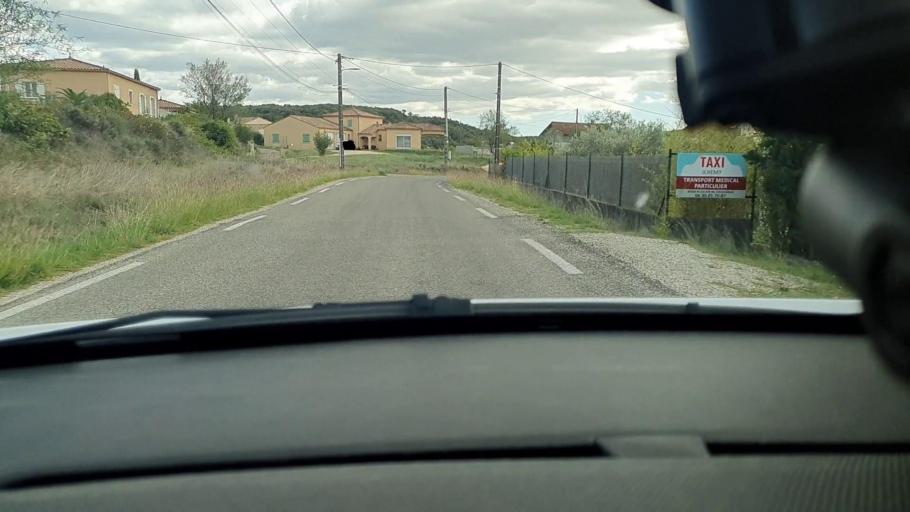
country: FR
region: Languedoc-Roussillon
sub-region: Departement du Gard
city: Les Mages
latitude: 44.2241
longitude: 4.1728
